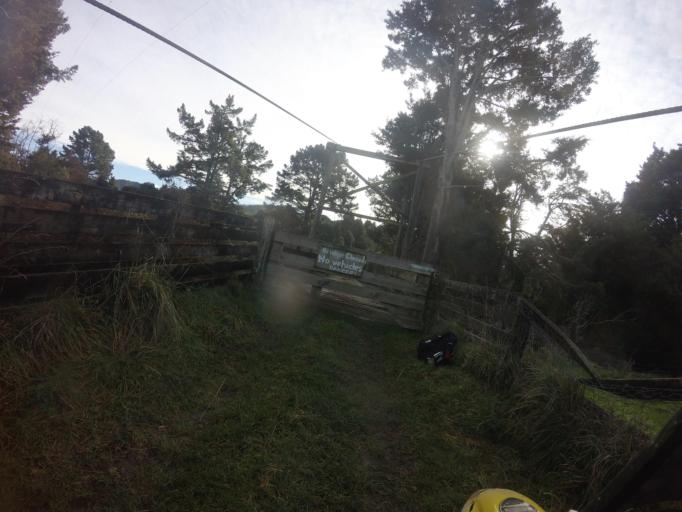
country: NZ
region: Hawke's Bay
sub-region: Wairoa District
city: Wairoa
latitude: -38.9457
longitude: 177.5936
